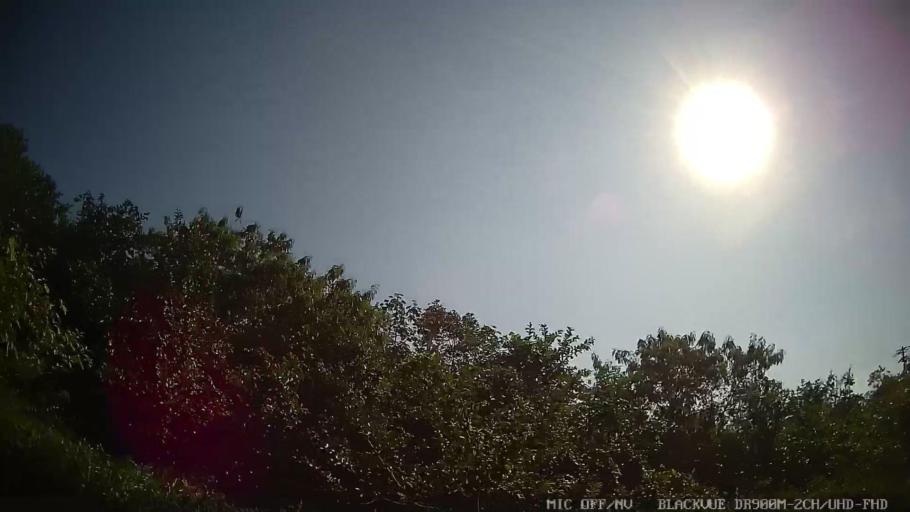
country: BR
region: Sao Paulo
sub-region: Guaruja
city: Guaruja
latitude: -24.0041
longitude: -46.2874
